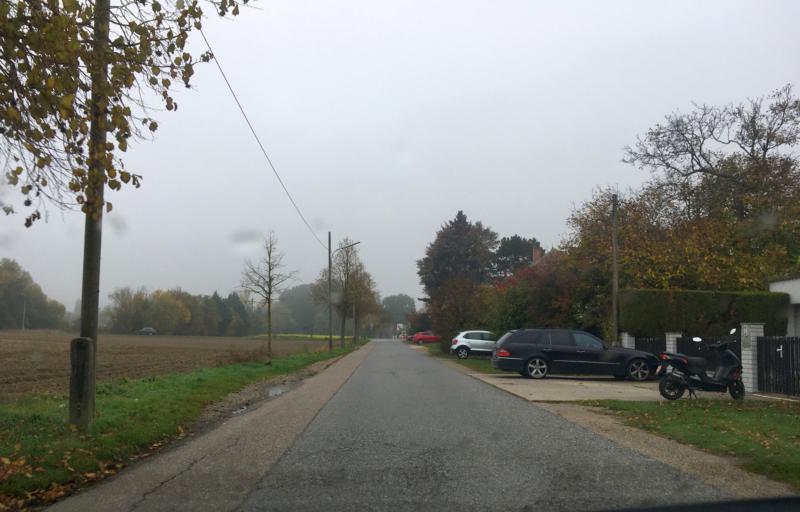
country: AT
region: Lower Austria
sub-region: Politischer Bezirk Ganserndorf
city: Gross-Enzersdorf
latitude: 48.2065
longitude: 16.4878
